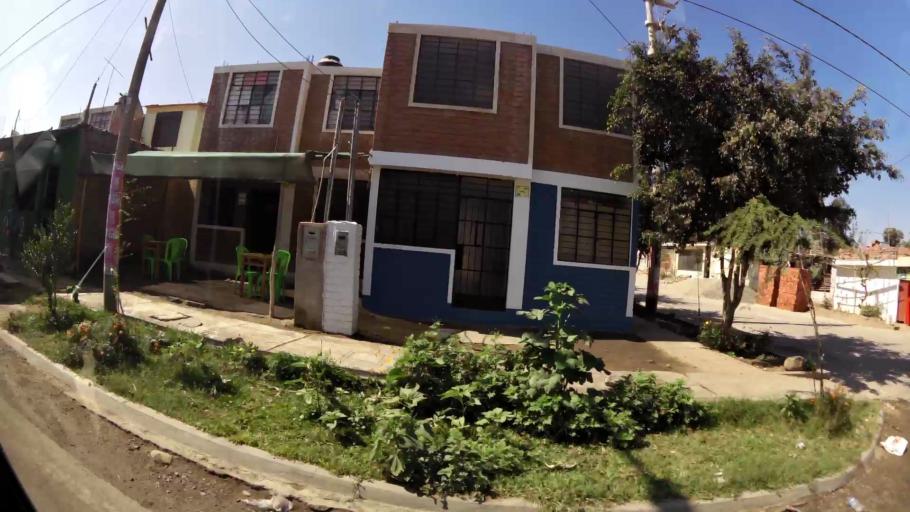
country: PE
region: Ica
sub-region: Provincia de Ica
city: Guadalupe
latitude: -13.9308
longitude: -75.6698
